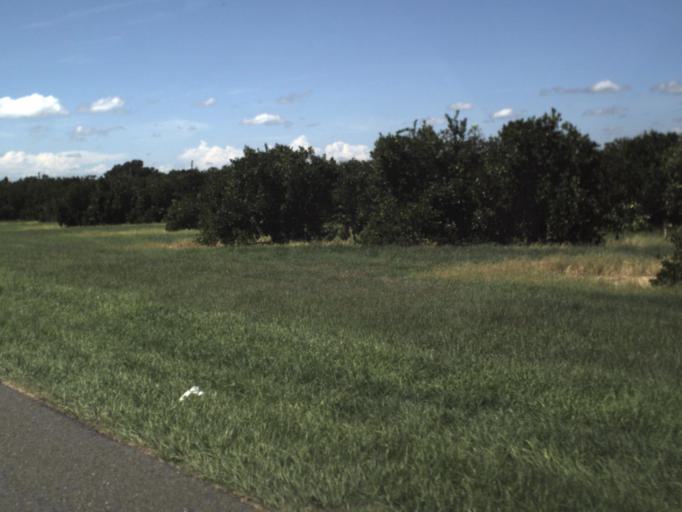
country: US
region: Florida
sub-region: Polk County
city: Lake Wales
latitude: 27.9460
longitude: -81.5950
